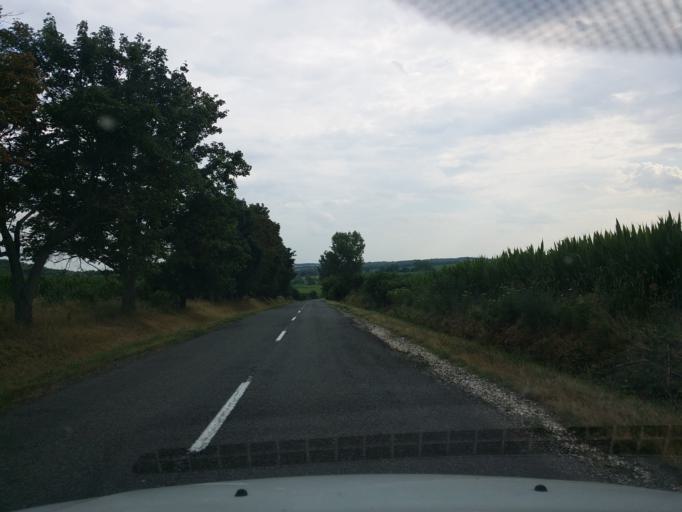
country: HU
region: Nograd
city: Bercel
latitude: 47.9023
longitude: 19.3721
